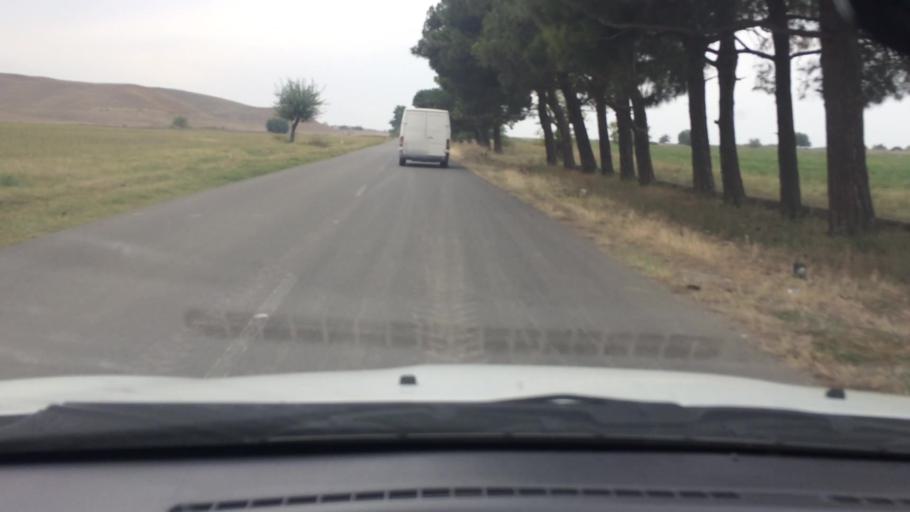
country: AM
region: Tavush
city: Berdavan
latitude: 41.3355
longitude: 45.0253
